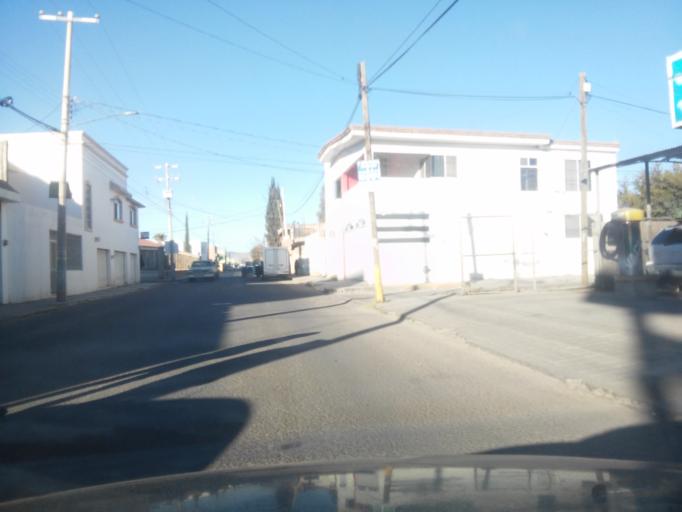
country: MX
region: Durango
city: Victoria de Durango
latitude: 24.0135
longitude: -104.6452
